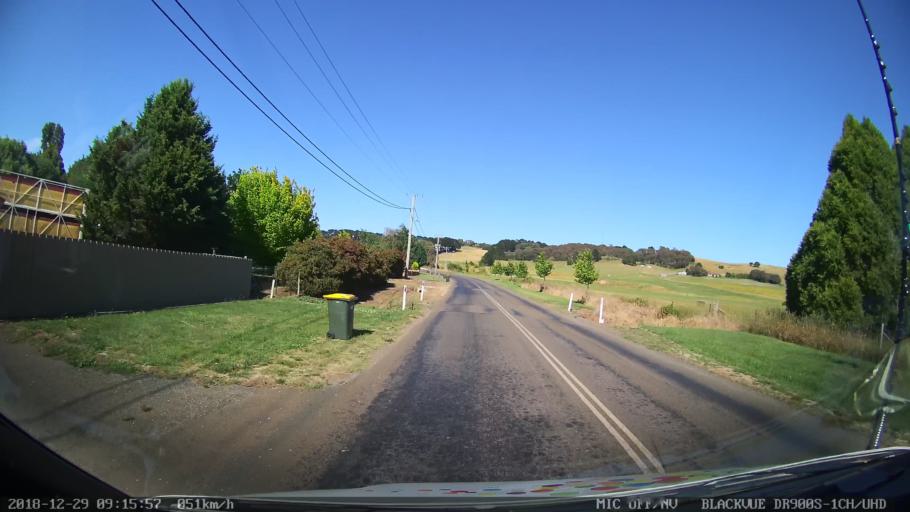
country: AU
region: New South Wales
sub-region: Upper Lachlan Shire
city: Crookwell
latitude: -34.4559
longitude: 149.4558
